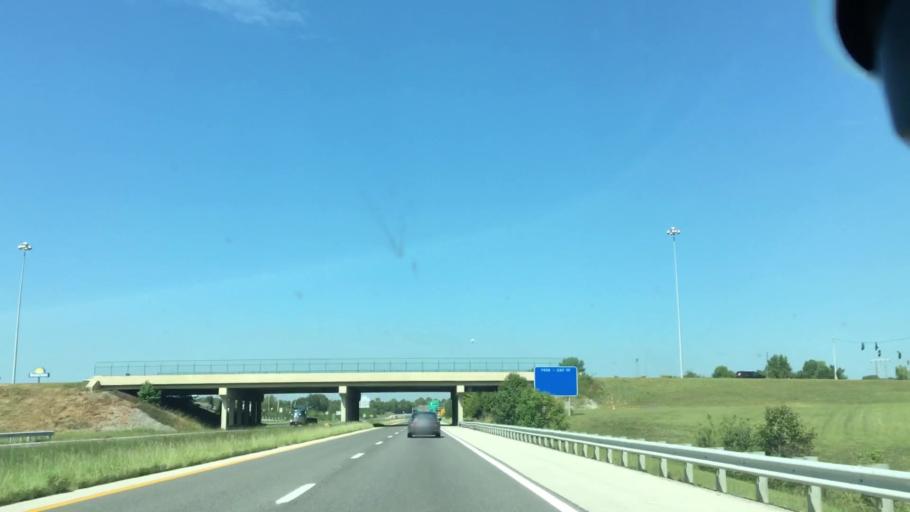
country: US
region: Kentucky
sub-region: Hopkins County
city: Madisonville
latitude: 37.3518
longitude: -87.4858
